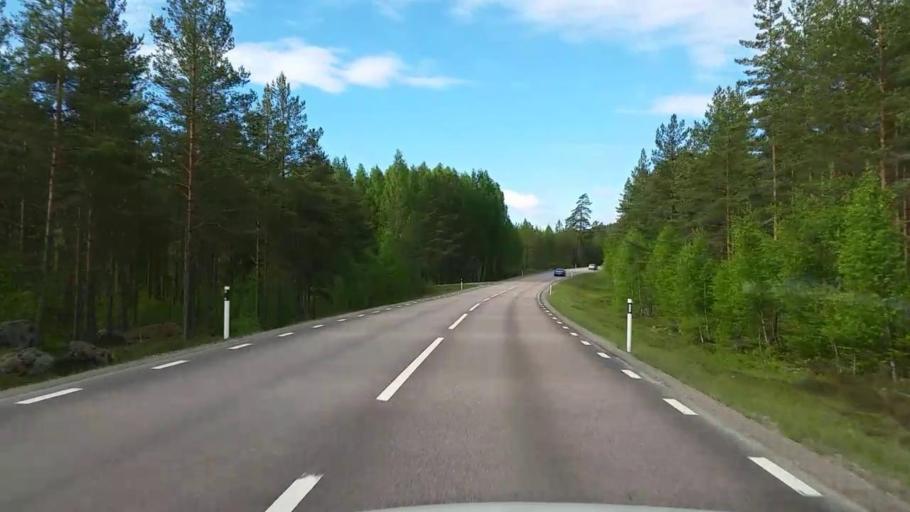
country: SE
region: Dalarna
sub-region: Faluns Kommun
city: Falun
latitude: 60.6864
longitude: 15.7231
